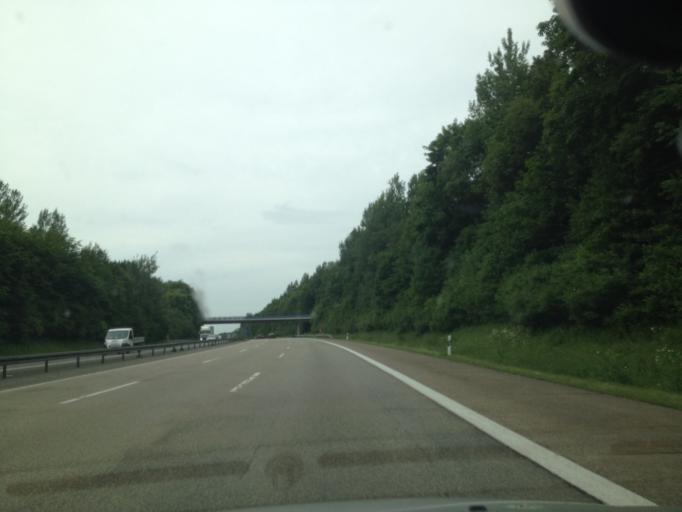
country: DE
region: North Rhine-Westphalia
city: Meinerzhagen
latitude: 51.0901
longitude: 7.6871
